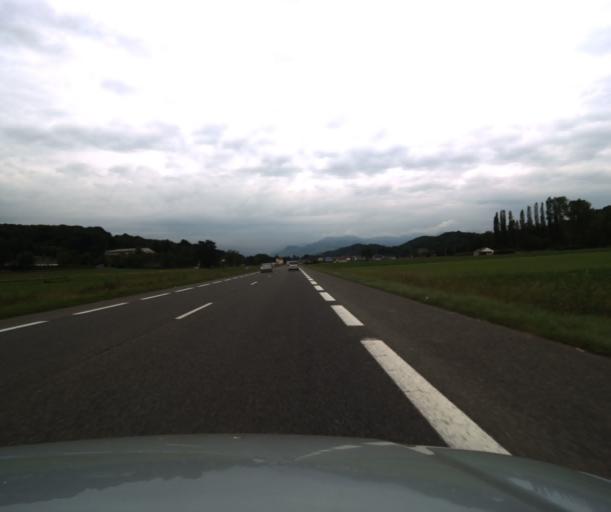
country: FR
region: Midi-Pyrenees
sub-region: Departement des Hautes-Pyrenees
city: Ossun
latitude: 43.1479
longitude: -0.0240
